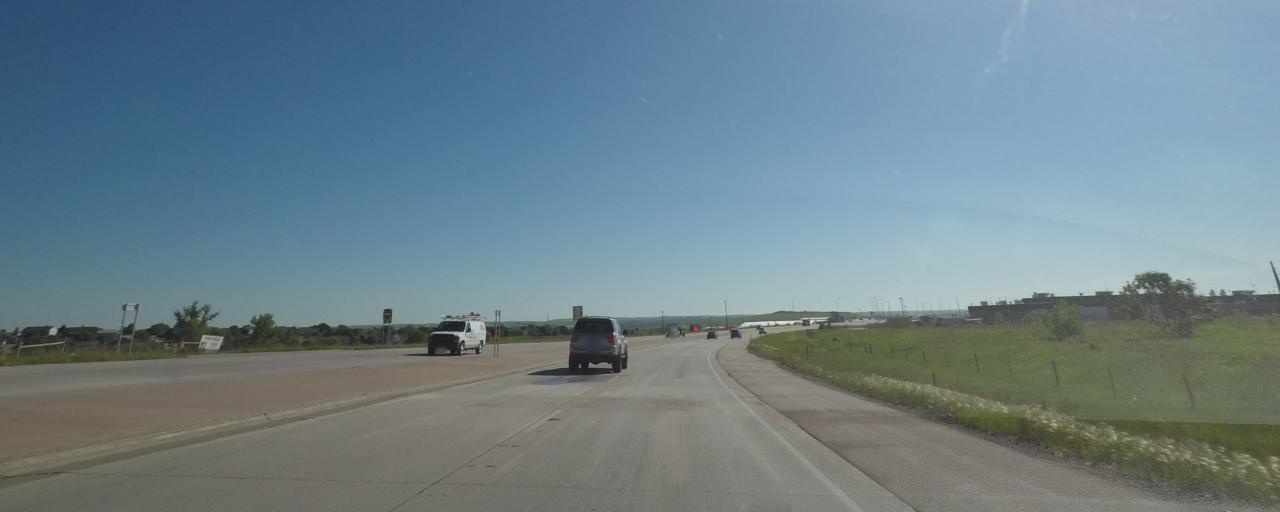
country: US
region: South Dakota
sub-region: Pennington County
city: Rapid City
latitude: 44.0367
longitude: -103.2008
